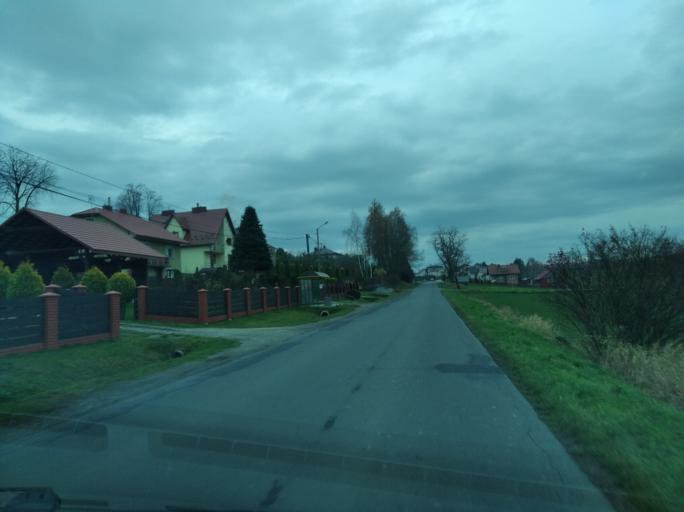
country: PL
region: Subcarpathian Voivodeship
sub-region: Powiat ropczycko-sedziszowski
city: Iwierzyce
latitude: 50.0182
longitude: 21.7526
